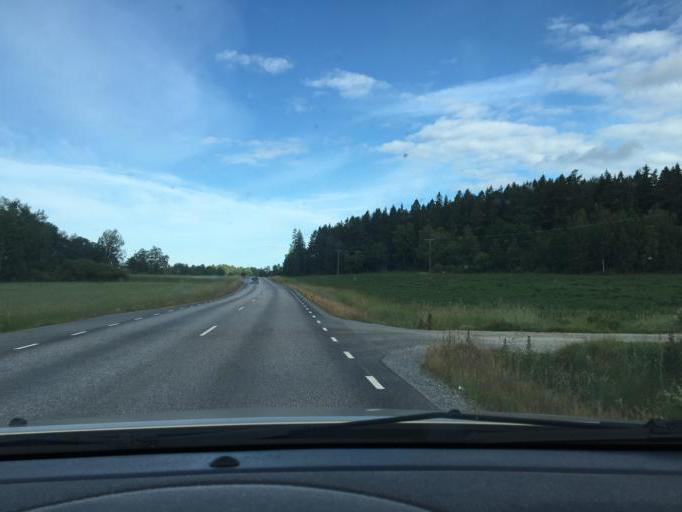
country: SE
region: Stockholm
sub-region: Salems Kommun
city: Ronninge
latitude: 59.2273
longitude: 17.7282
